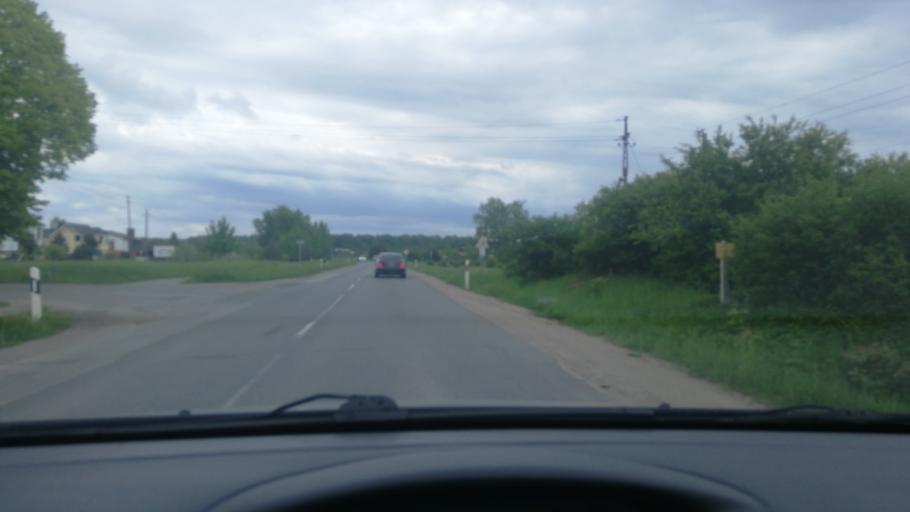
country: LT
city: Priekule
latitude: 55.6424
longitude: 21.2926
